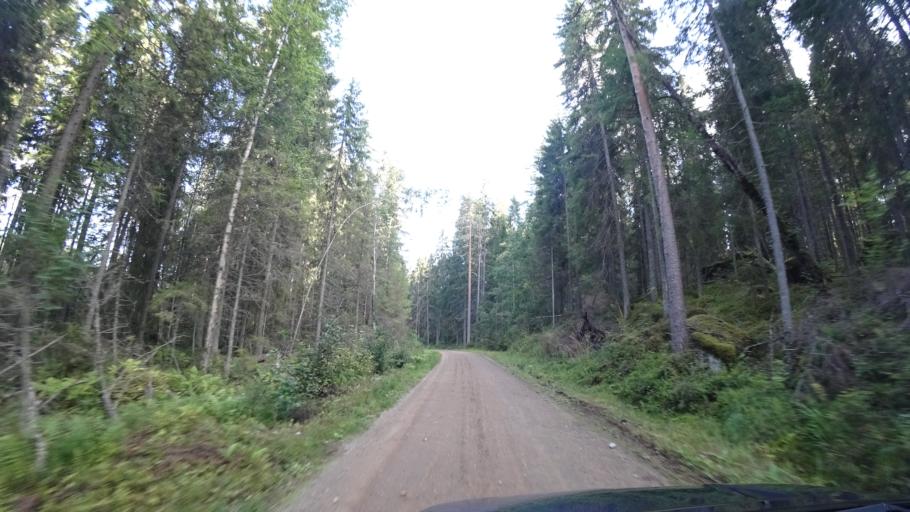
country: FI
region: Paijanne Tavastia
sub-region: Lahti
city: Auttoinen
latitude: 61.2209
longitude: 25.2030
